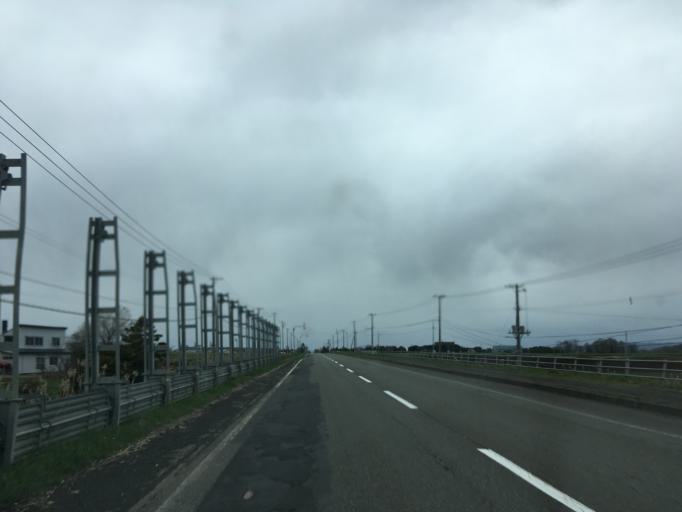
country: JP
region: Hokkaido
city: Chitose
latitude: 42.9259
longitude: 141.8079
